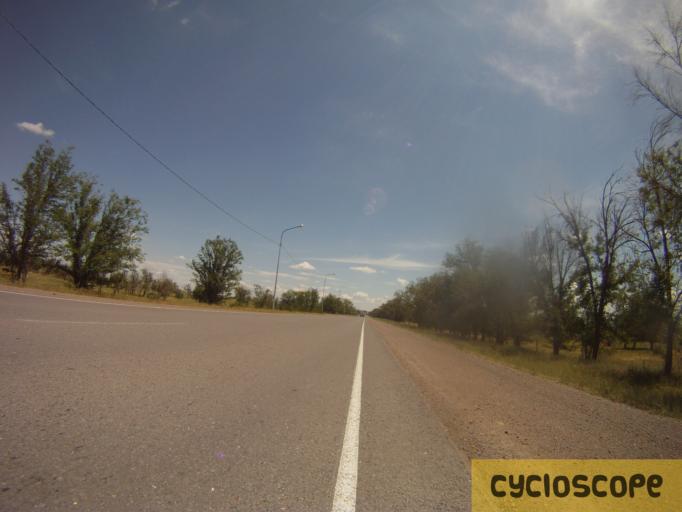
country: KG
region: Chuy
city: Bystrovka
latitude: 43.3208
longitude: 76.0239
